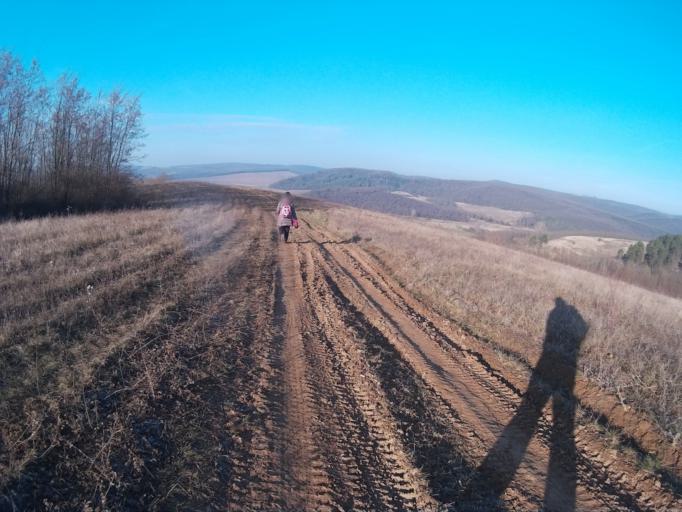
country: HU
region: Nograd
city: Bercel
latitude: 47.9692
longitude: 19.4400
